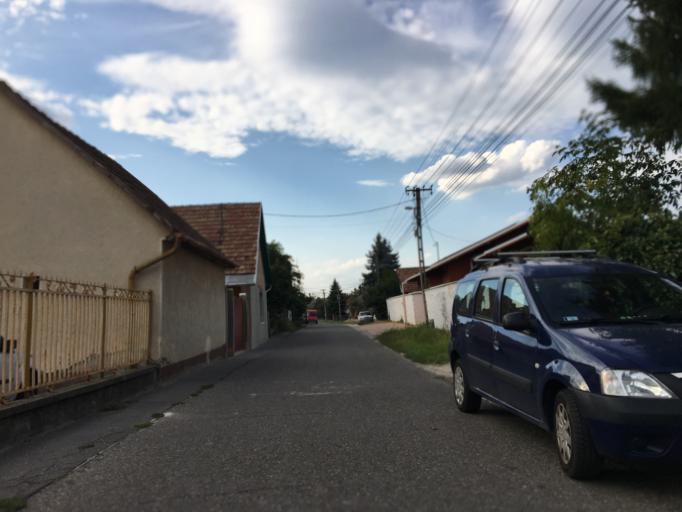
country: HU
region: Pest
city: Szigetszentmiklos
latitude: 47.3541
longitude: 19.0301
